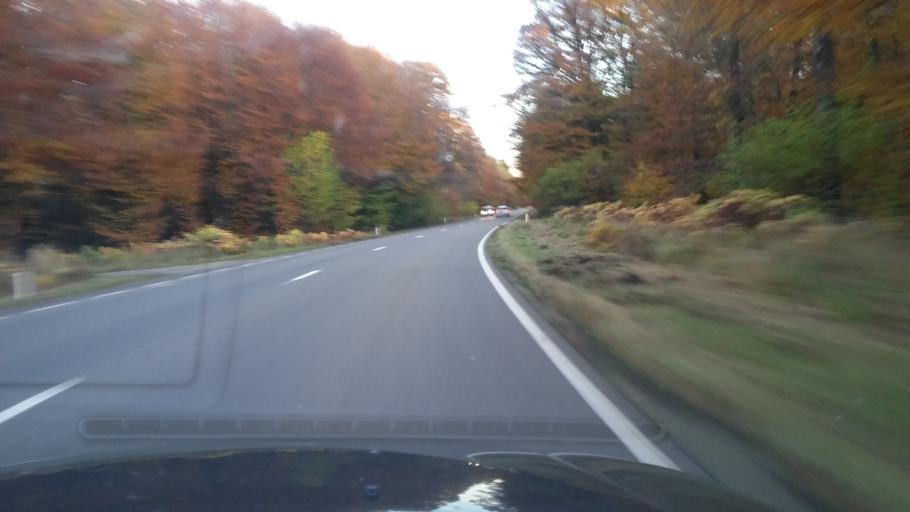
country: BE
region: Wallonia
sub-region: Province du Luxembourg
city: Herbeumont
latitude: 49.7554
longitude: 5.2026
